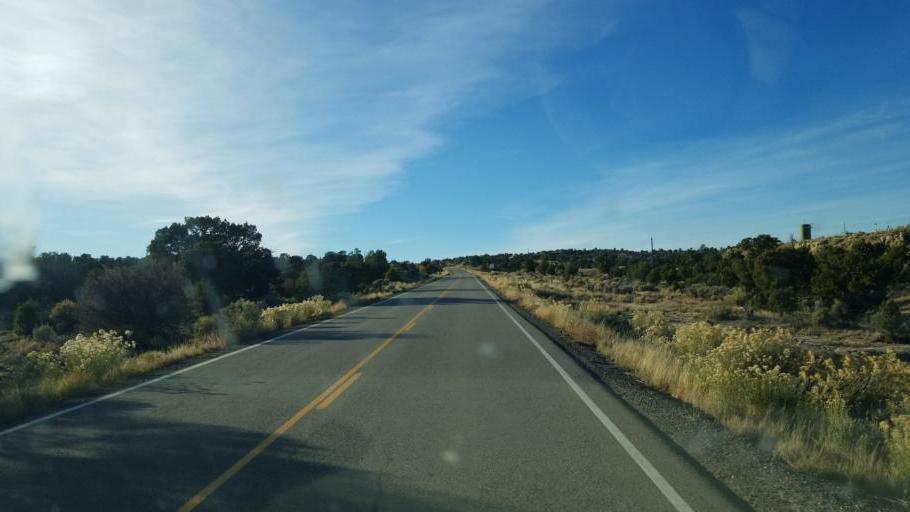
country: US
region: New Mexico
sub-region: San Juan County
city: Bloomfield
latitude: 36.7283
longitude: -107.6727
